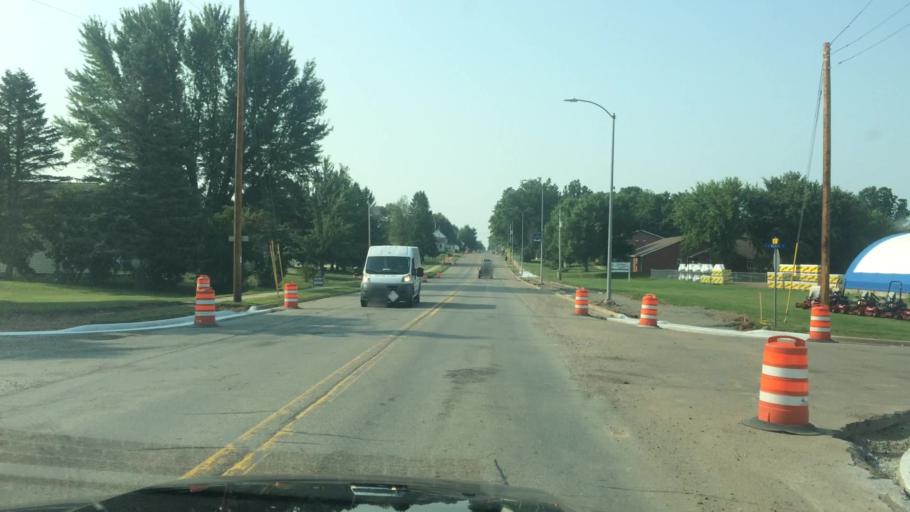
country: US
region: Wisconsin
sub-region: Marathon County
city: Stratford
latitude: 44.8083
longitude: -90.0793
